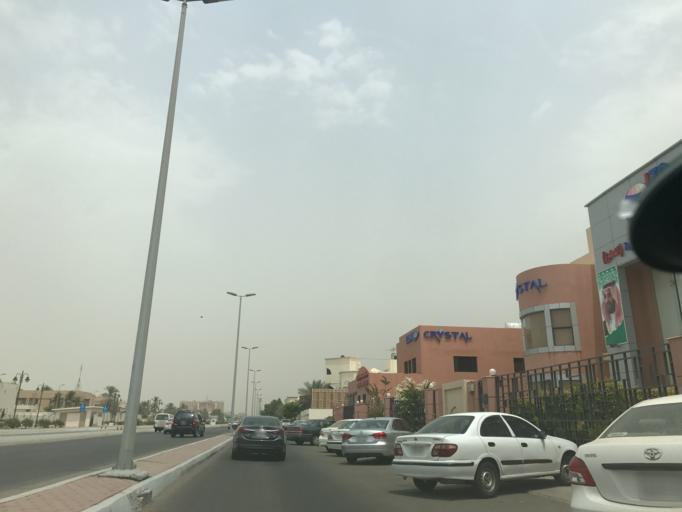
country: SA
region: Makkah
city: Jeddah
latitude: 21.5546
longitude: 39.1610
